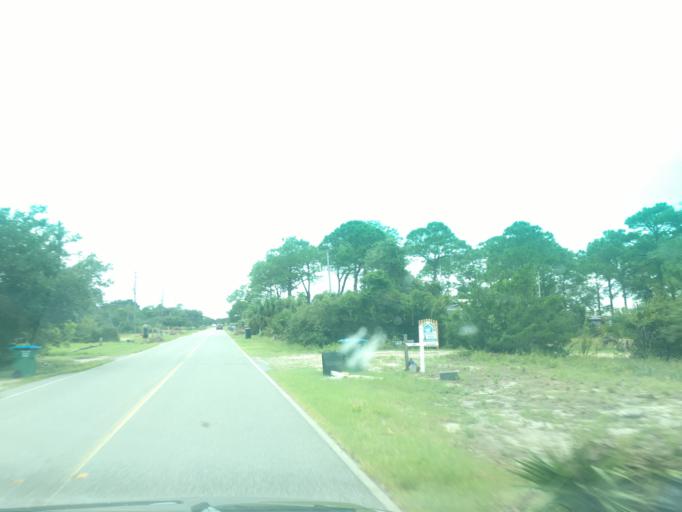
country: US
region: Florida
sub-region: Franklin County
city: Carrabelle
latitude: 29.8980
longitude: -84.3909
